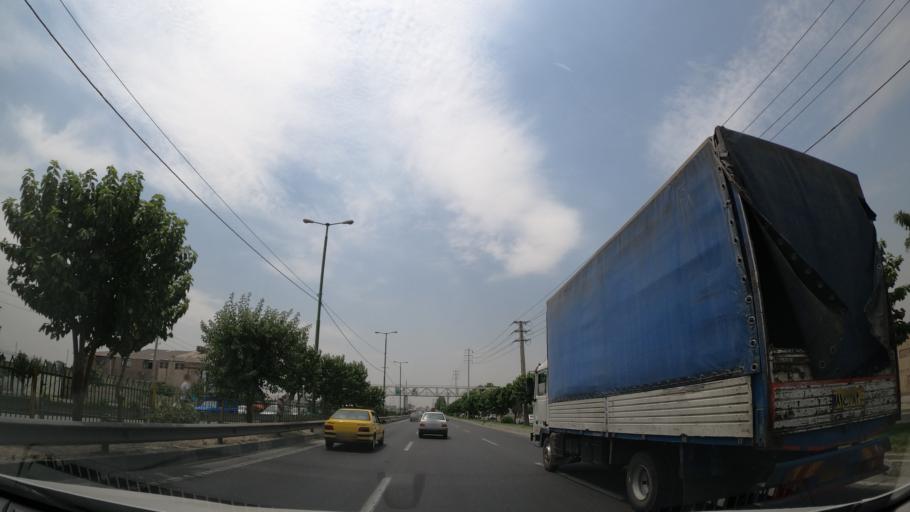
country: IR
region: Tehran
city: Eslamshahr
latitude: 35.6766
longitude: 51.2836
